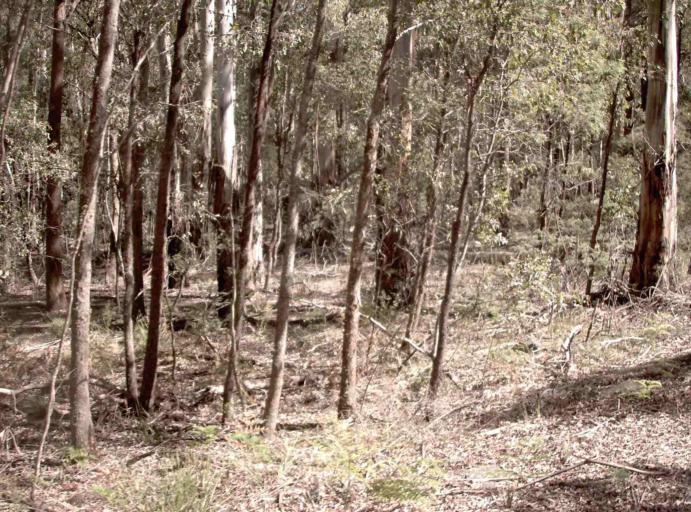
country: AU
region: New South Wales
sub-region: Bombala
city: Bombala
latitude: -37.1202
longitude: 148.7520
